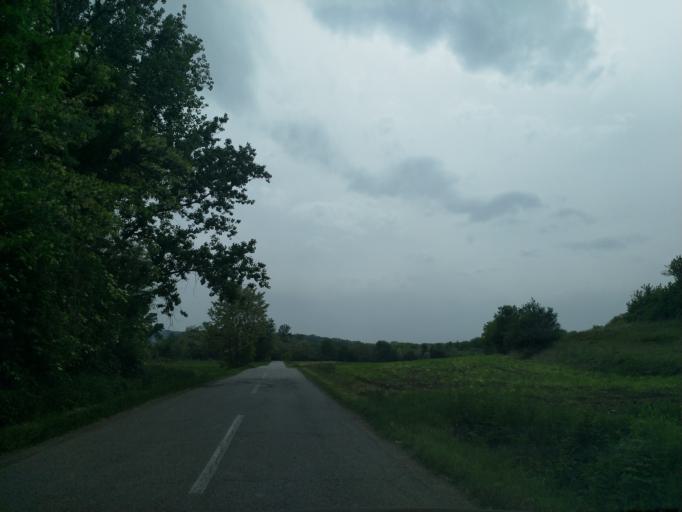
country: RS
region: Central Serbia
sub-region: Pomoravski Okrug
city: Paracin
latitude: 43.8689
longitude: 21.5411
